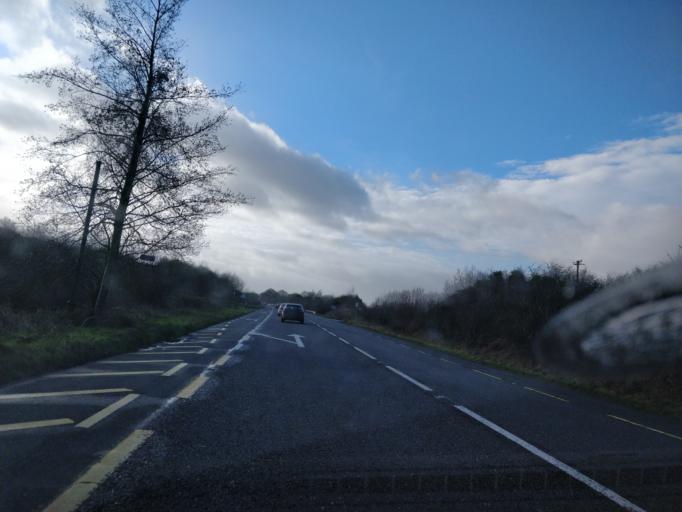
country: IE
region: Connaught
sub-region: Maigh Eo
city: Castlebar
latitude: 53.8787
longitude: -9.2230
